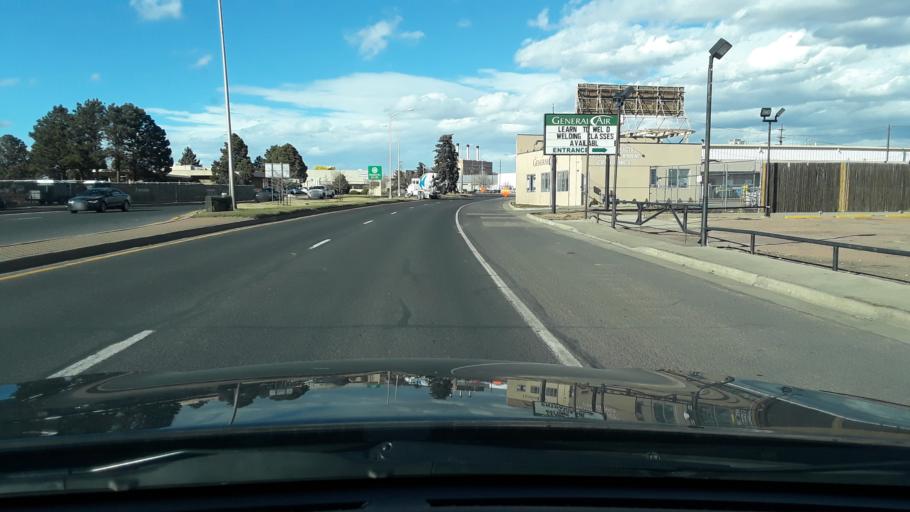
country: US
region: Colorado
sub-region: El Paso County
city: Colorado Springs
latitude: 38.8754
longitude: -104.8193
